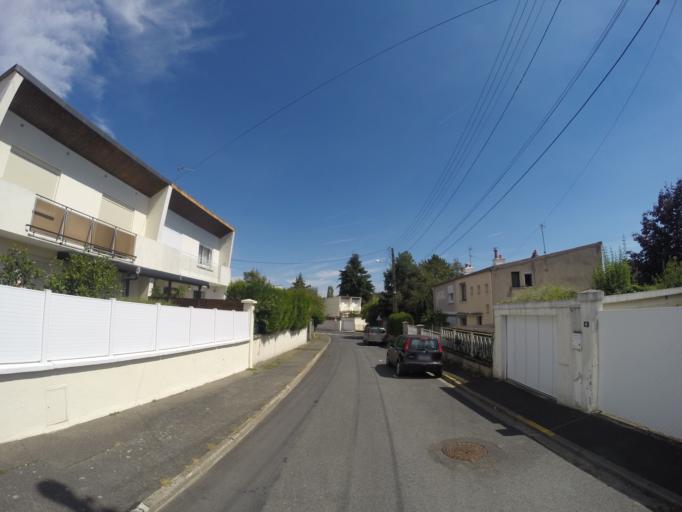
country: FR
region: Centre
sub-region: Departement d'Indre-et-Loire
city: Tours
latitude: 47.4085
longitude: 0.7136
